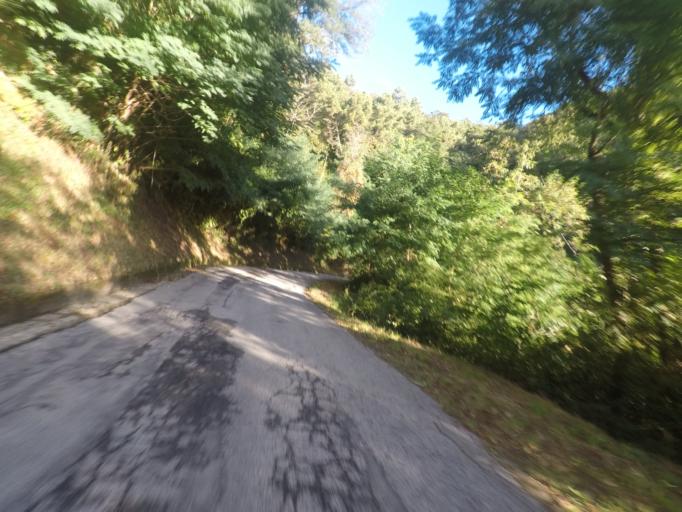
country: IT
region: Tuscany
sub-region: Provincia di Lucca
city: Stiava
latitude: 43.9145
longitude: 10.3667
